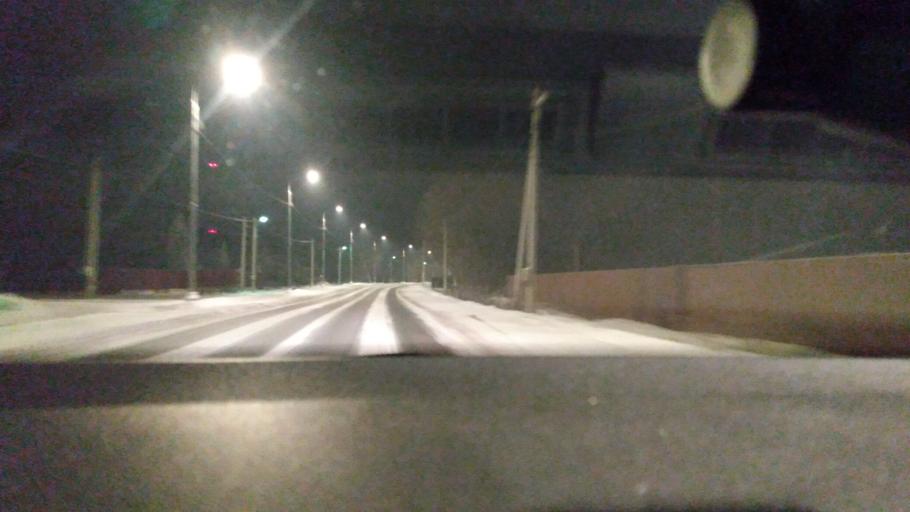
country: RU
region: Moskovskaya
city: Krasnaya Poyma
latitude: 55.1043
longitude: 38.9983
